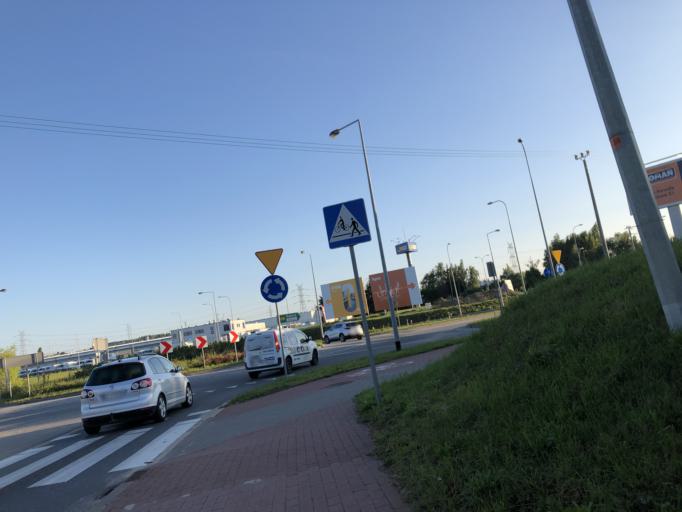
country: PL
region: Pomeranian Voivodeship
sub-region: Powiat gdanski
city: Rotmanka
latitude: 54.2817
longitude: 18.5944
